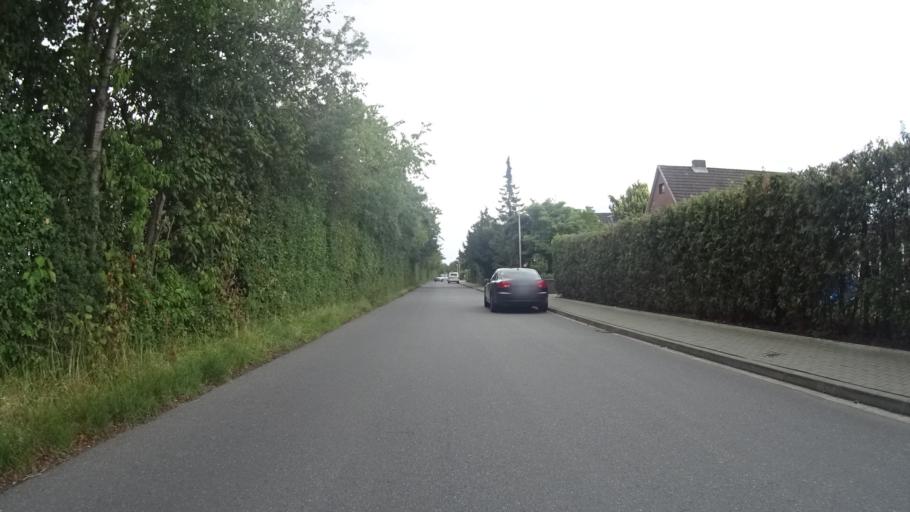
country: DE
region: Schleswig-Holstein
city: Gluckstadt
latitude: 53.7838
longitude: 9.4386
